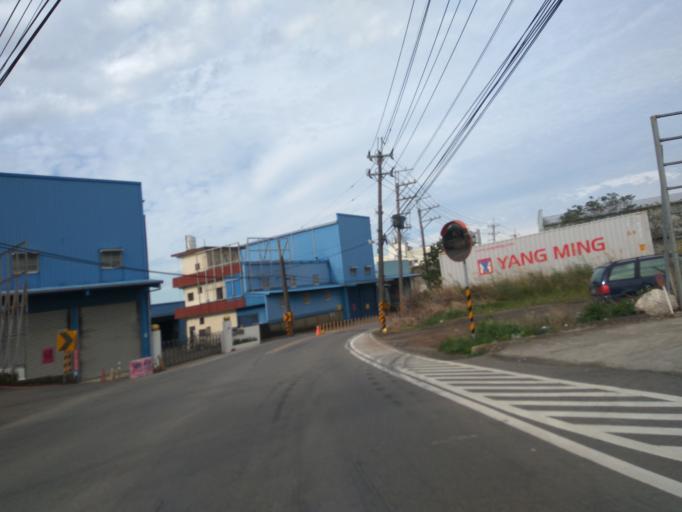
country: TW
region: Taiwan
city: Daxi
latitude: 24.9374
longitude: 121.1635
